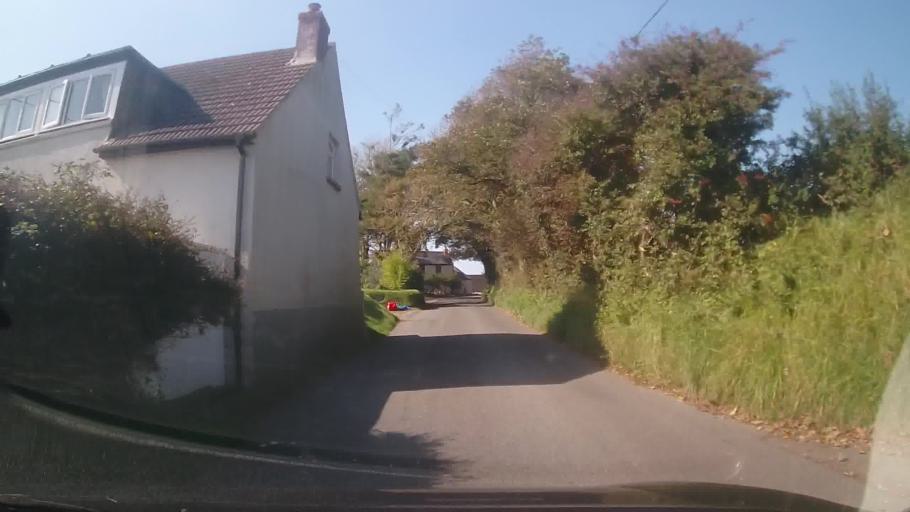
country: GB
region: Wales
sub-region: Pembrokeshire
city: Camrose
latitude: 51.8418
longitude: -4.9977
